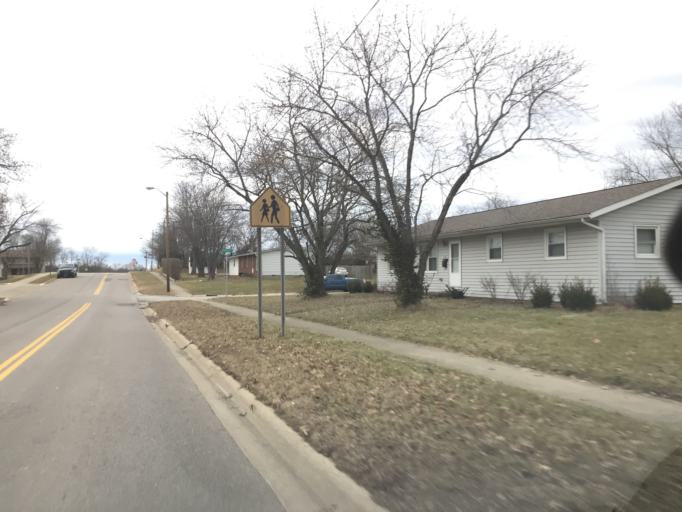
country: US
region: Indiana
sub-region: Monroe County
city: Bloomington
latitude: 39.1746
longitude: -86.5472
